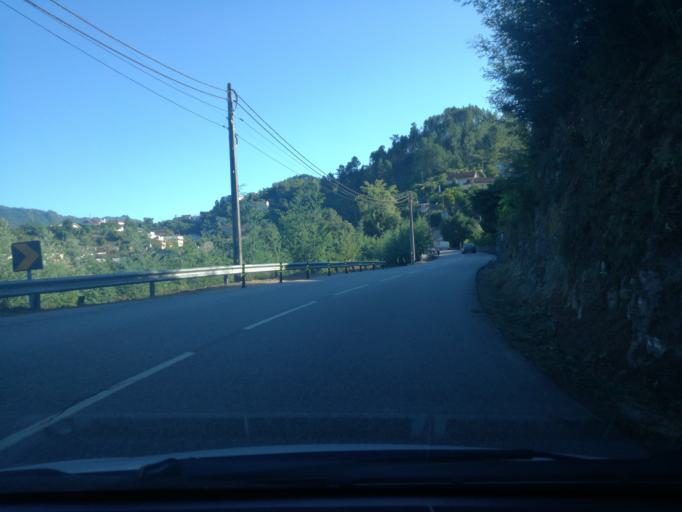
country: PT
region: Braga
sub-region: Vieira do Minho
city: Real
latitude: 41.6815
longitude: -8.1735
